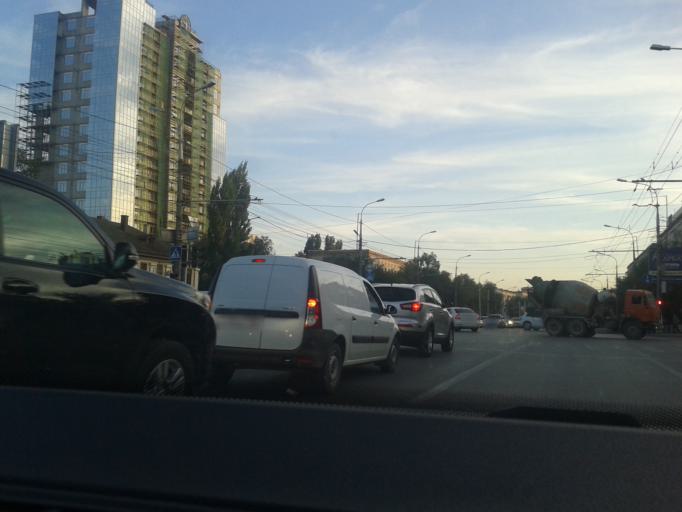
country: RU
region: Volgograd
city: Volgograd
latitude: 48.7247
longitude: 44.5364
